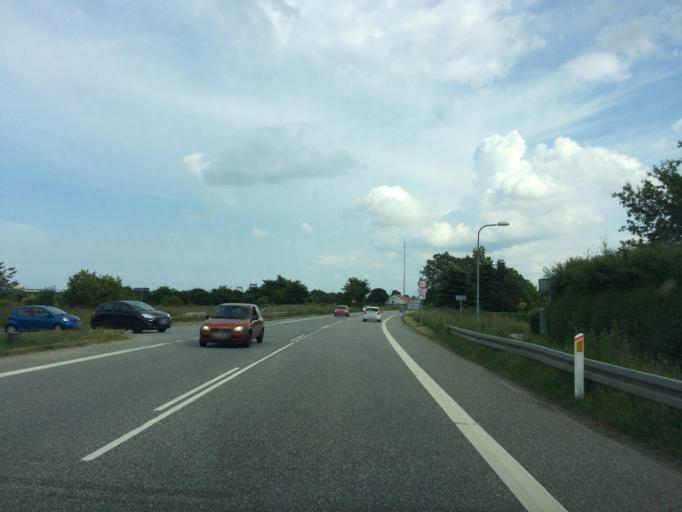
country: DK
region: South Denmark
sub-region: Fredericia Kommune
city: Snoghoj
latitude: 55.5316
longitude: 9.7035
